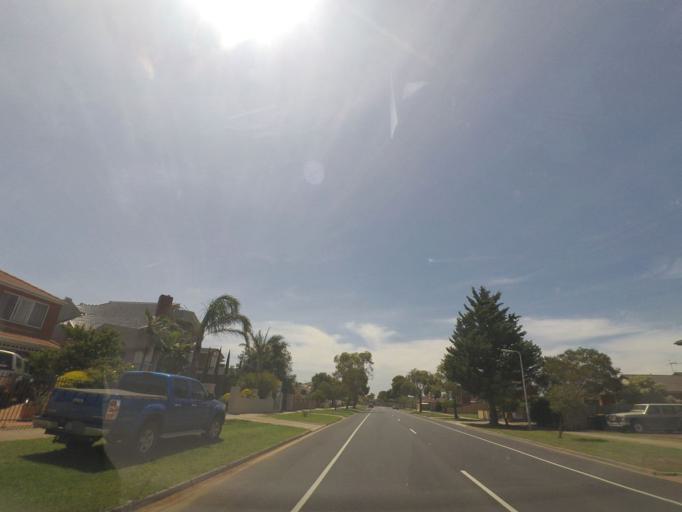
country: AU
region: Victoria
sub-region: Brimbank
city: Delahey
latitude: -37.7141
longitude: 144.7895
